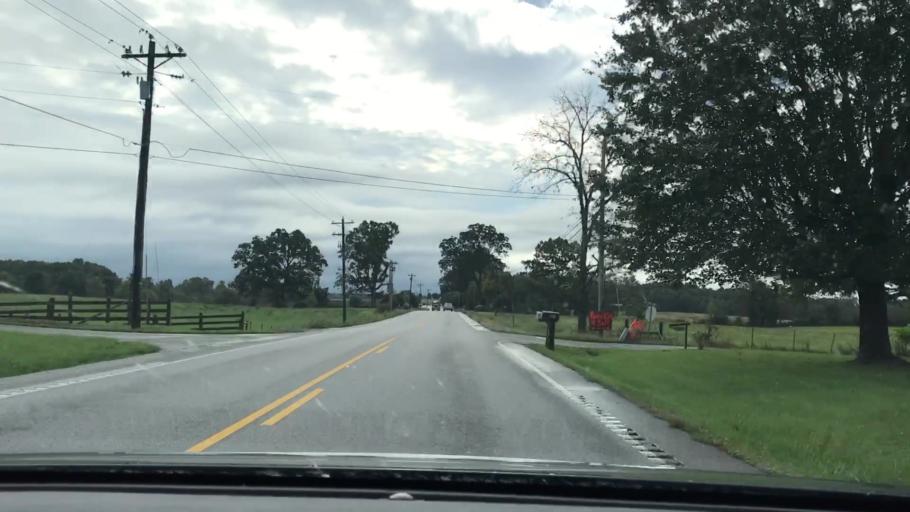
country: US
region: Tennessee
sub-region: Fentress County
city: Jamestown
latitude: 36.3629
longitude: -84.8411
